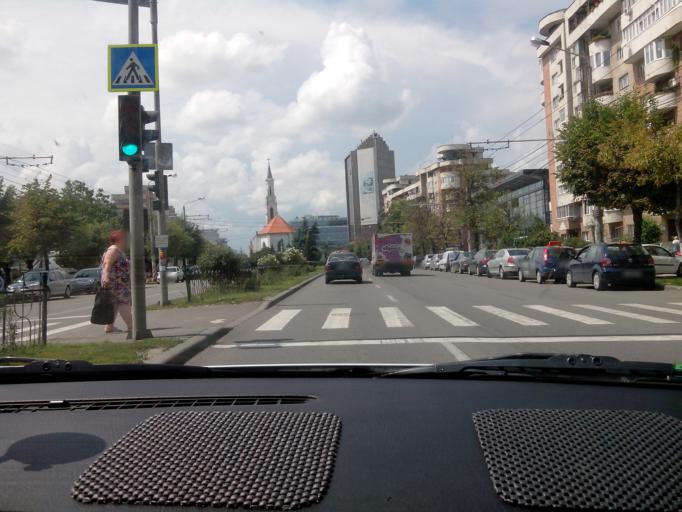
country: RO
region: Cluj
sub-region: Municipiul Cluj-Napoca
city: Cluj-Napoca
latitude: 46.7775
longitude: 23.6099
